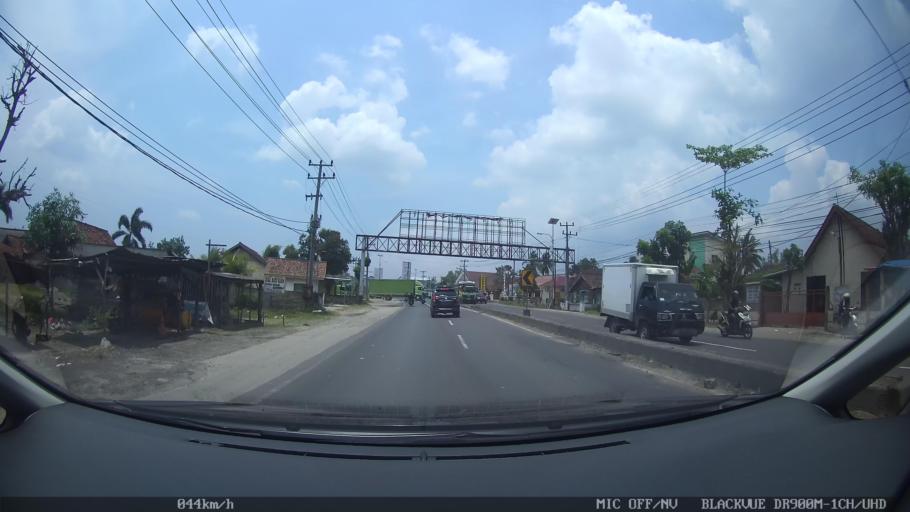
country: ID
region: Lampung
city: Natar
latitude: -5.3037
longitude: 105.1918
